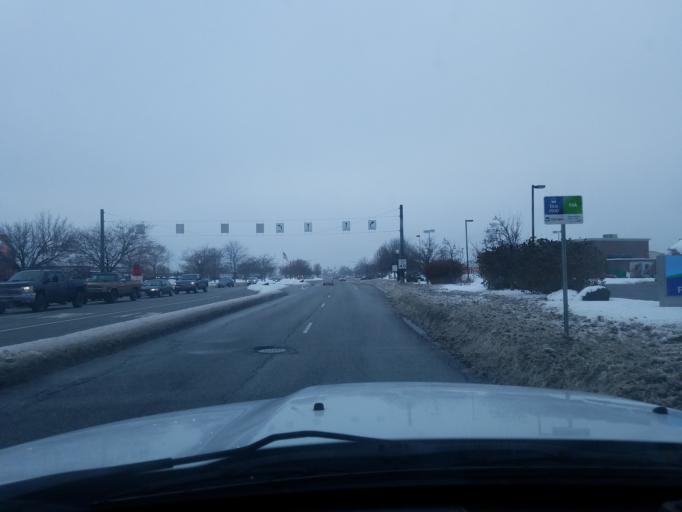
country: US
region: Indiana
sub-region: Saint Joseph County
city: Georgetown
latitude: 41.7125
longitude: -86.1791
